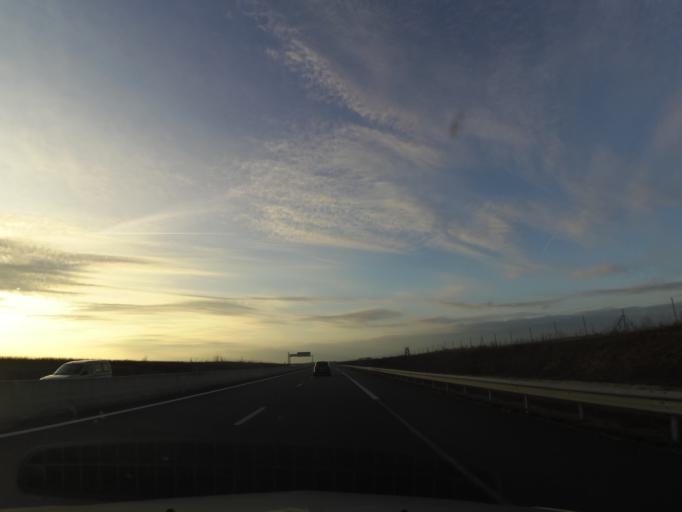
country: FR
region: Centre
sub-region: Departement du Loiret
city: Pannes
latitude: 48.0748
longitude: 2.6353
